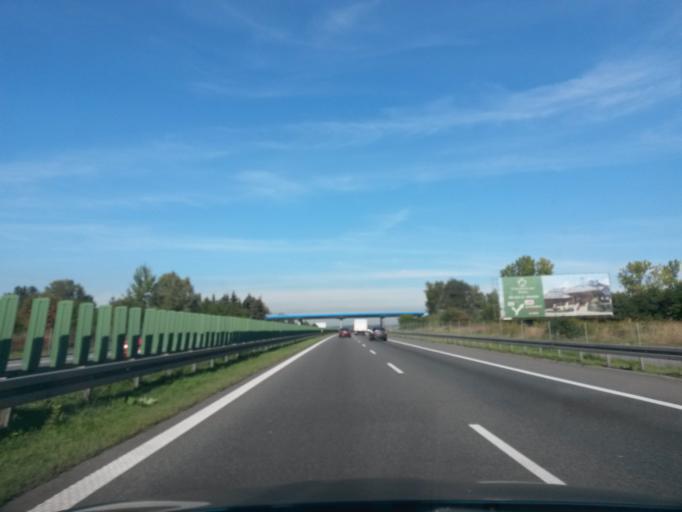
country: PL
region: Lesser Poland Voivodeship
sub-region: Powiat krakowski
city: Kryspinow
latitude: 50.0593
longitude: 19.8097
